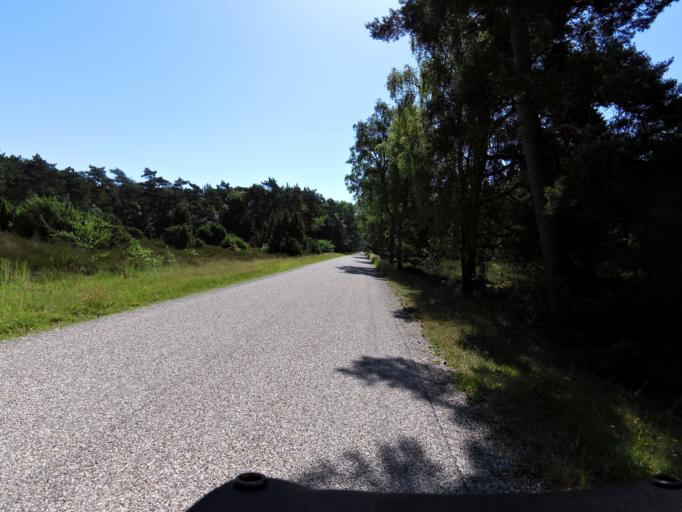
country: NL
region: Overijssel
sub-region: Gemeente Twenterand
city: Den Ham
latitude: 52.5380
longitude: 6.4902
